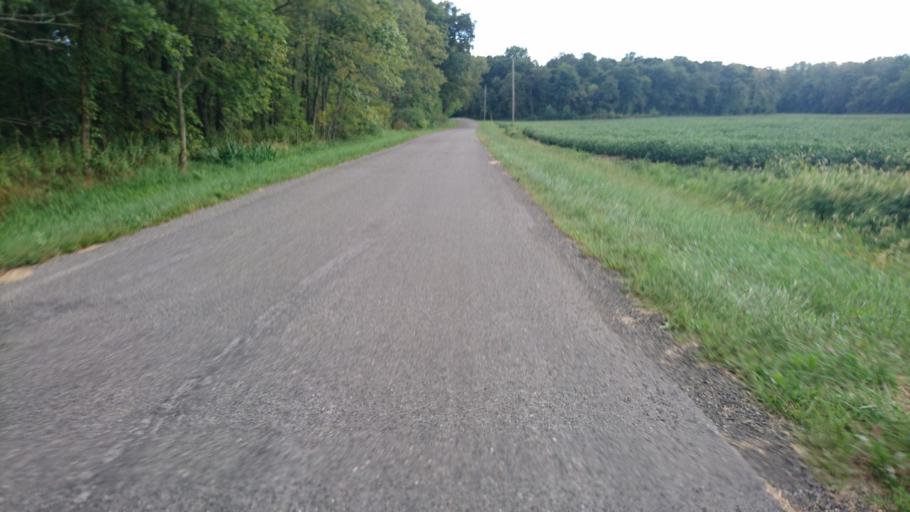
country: US
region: Illinois
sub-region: Macoupin County
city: Staunton
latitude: 38.9894
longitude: -89.7106
